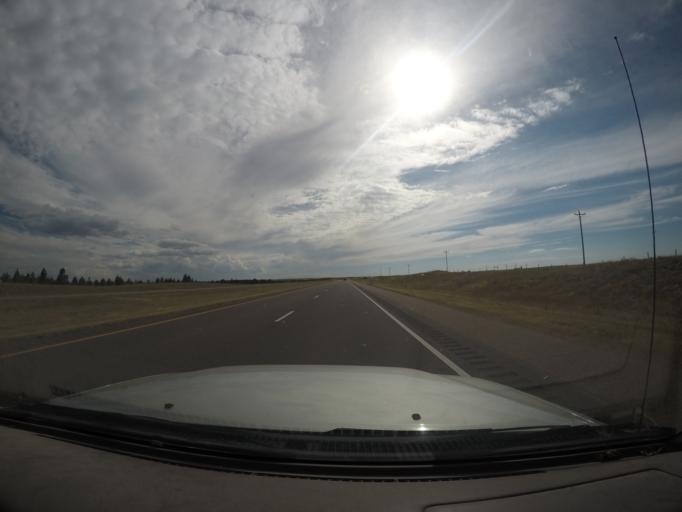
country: US
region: Nebraska
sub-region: Kimball County
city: Kimball
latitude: 41.1971
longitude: -103.7514
